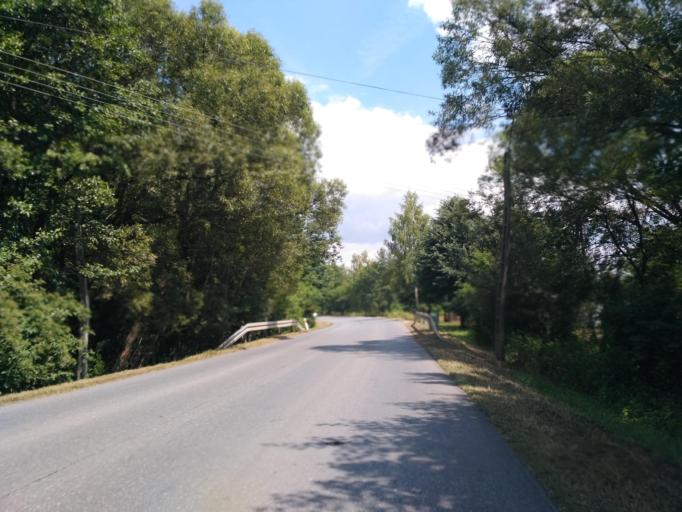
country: PL
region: Subcarpathian Voivodeship
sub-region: Powiat debicki
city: Pilzno
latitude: 50.0075
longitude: 21.2869
